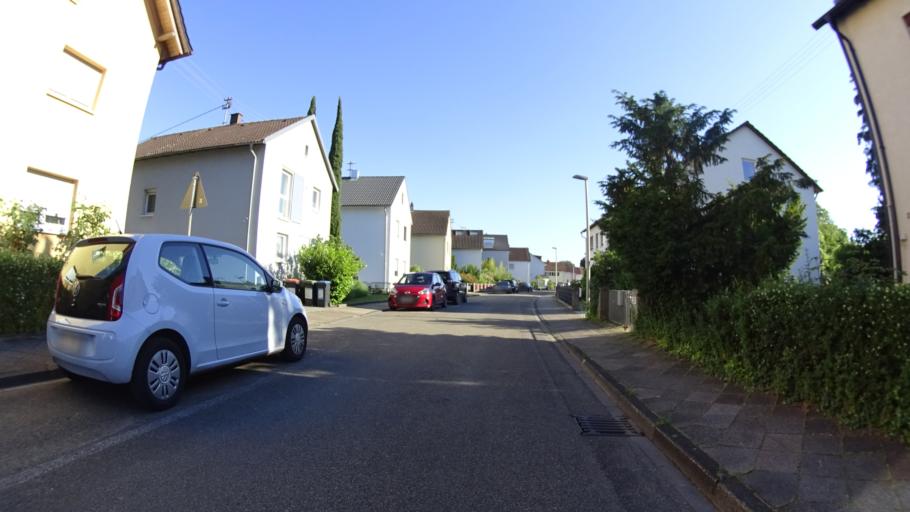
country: DE
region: Baden-Wuerttemberg
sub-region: Karlsruhe Region
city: Karlsruhe
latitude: 49.0301
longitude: 8.3685
